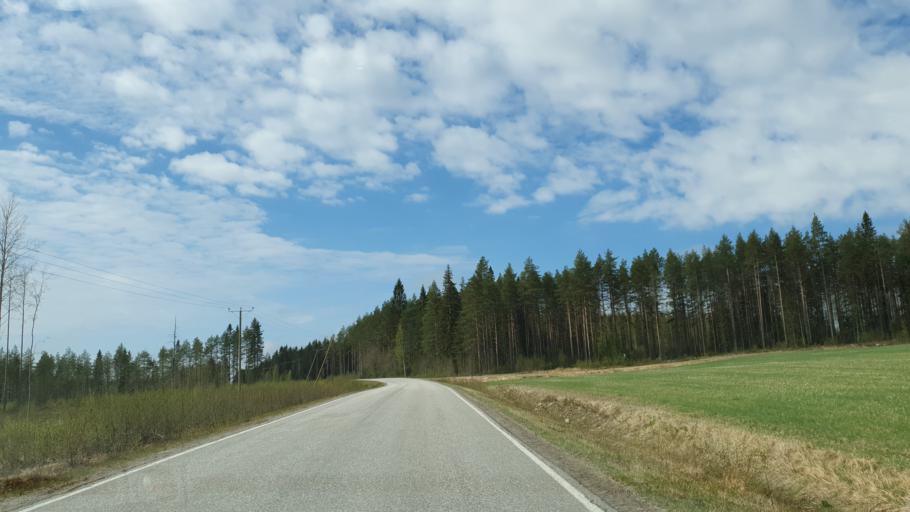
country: FI
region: Kainuu
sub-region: Kehys-Kainuu
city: Kuhmo
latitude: 64.1206
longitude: 29.6872
